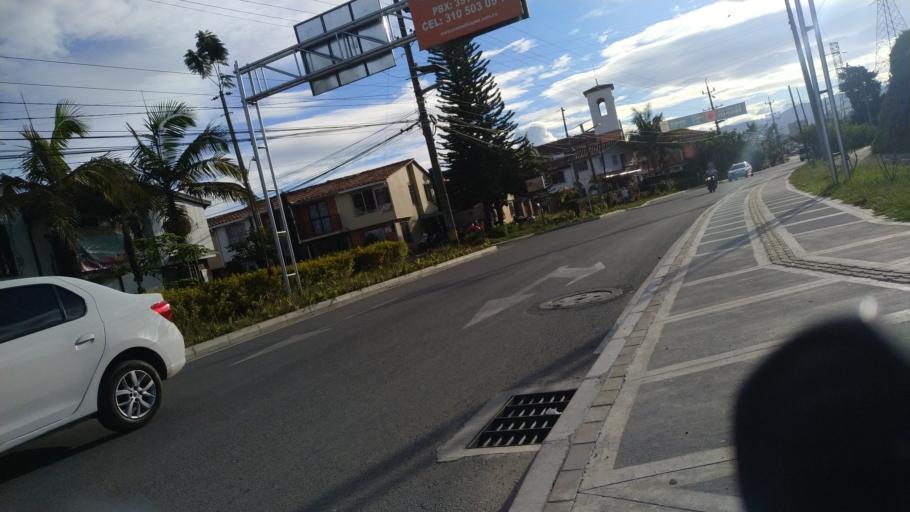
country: CO
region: Antioquia
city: Rionegro
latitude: 6.1475
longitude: -75.3799
